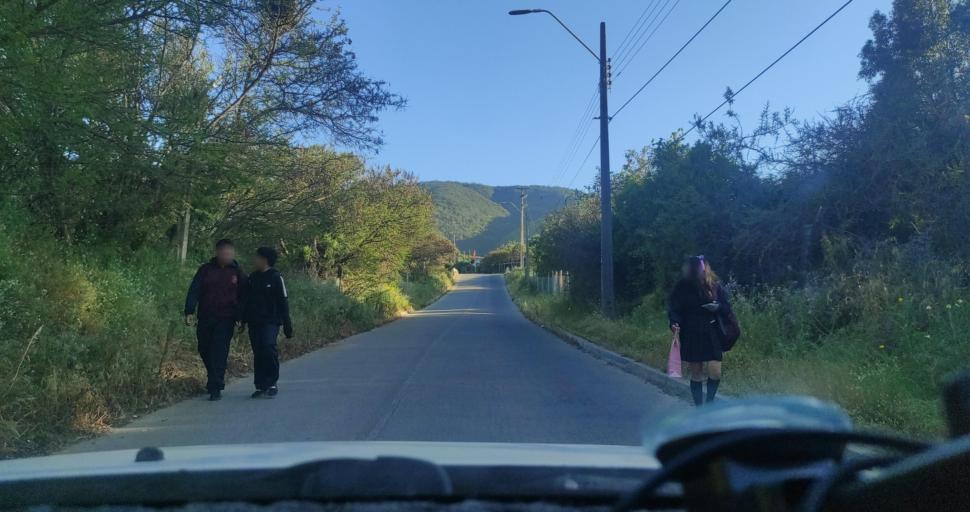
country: CL
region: Valparaiso
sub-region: Provincia de Marga Marga
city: Limache
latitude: -32.9911
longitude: -71.2356
